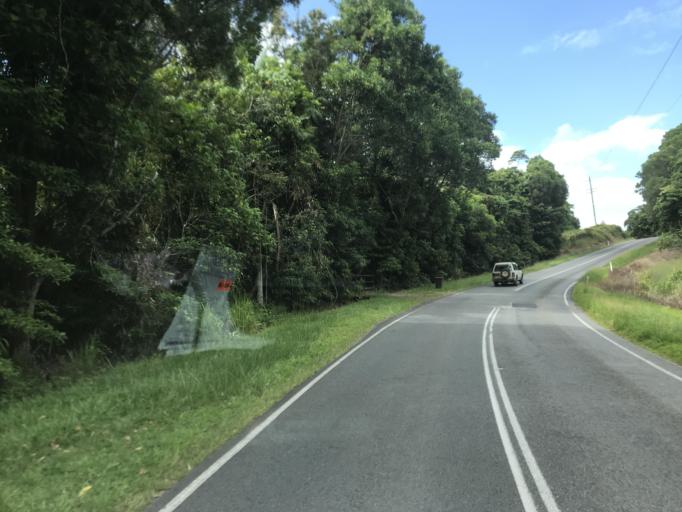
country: AU
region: Queensland
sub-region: Cassowary Coast
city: Innisfail
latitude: -17.8296
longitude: 146.0557
